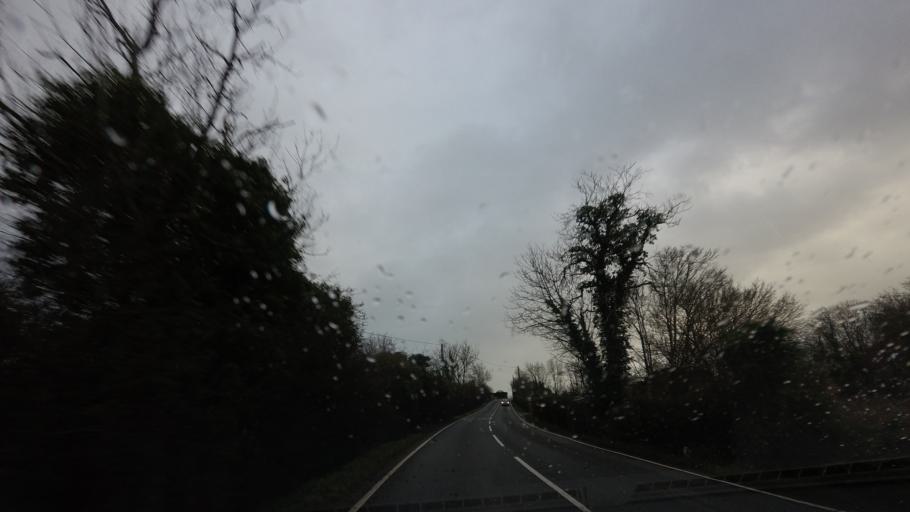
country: GB
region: England
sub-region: Kent
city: Staplehurst
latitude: 51.1975
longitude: 0.5275
